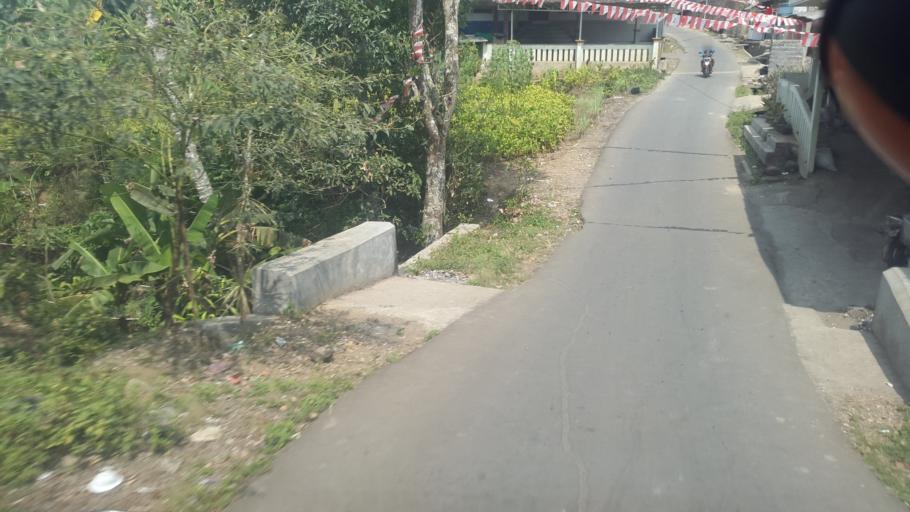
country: ID
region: West Java
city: Cicurug
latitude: -6.7593
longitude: 106.7416
